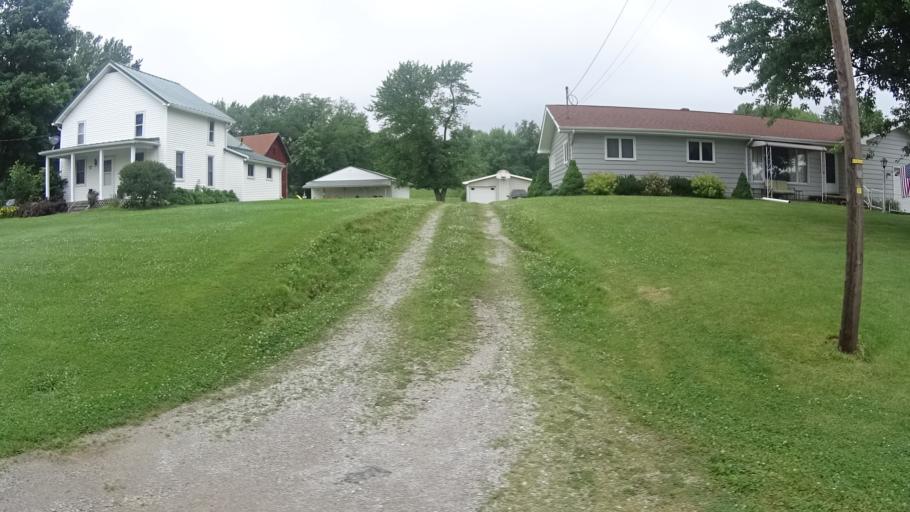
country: US
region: Ohio
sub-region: Erie County
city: Huron
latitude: 41.3252
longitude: -82.4848
